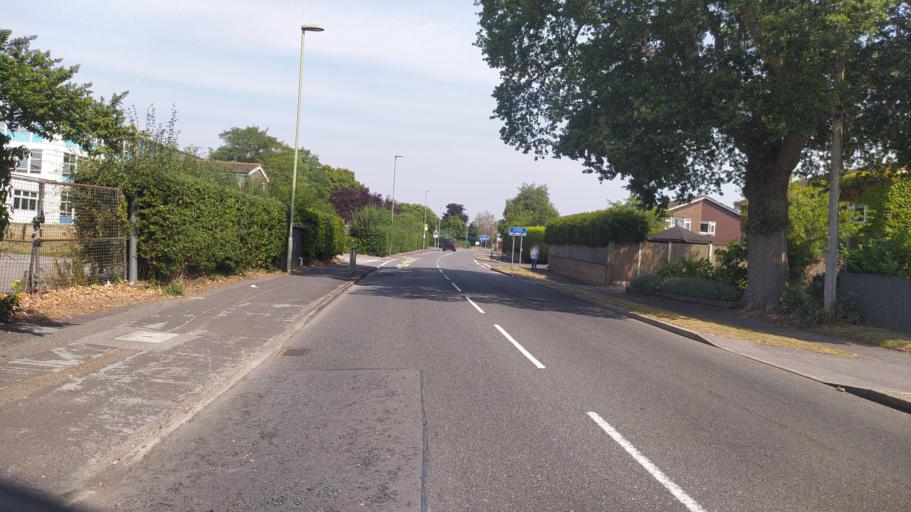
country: GB
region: England
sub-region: Hampshire
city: Havant
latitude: 50.8517
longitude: -0.9686
